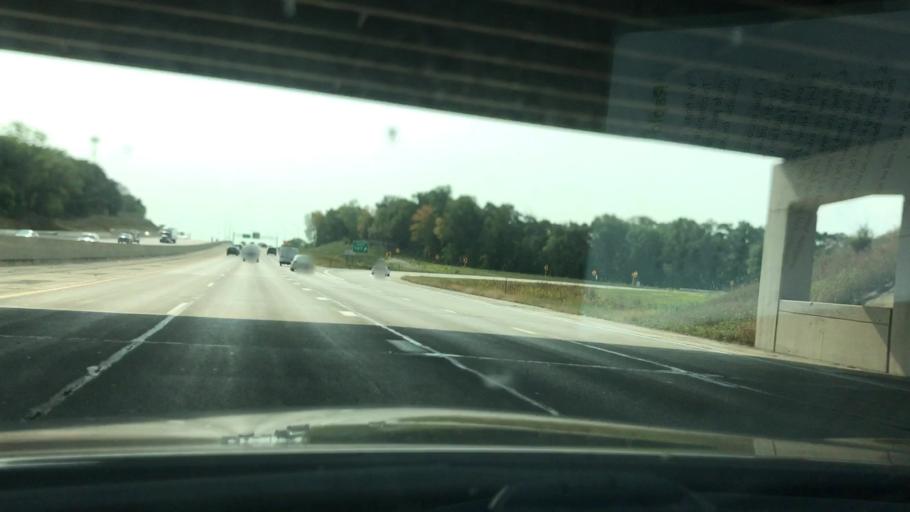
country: US
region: Michigan
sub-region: Livingston County
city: Brighton
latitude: 42.5322
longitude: -83.7665
